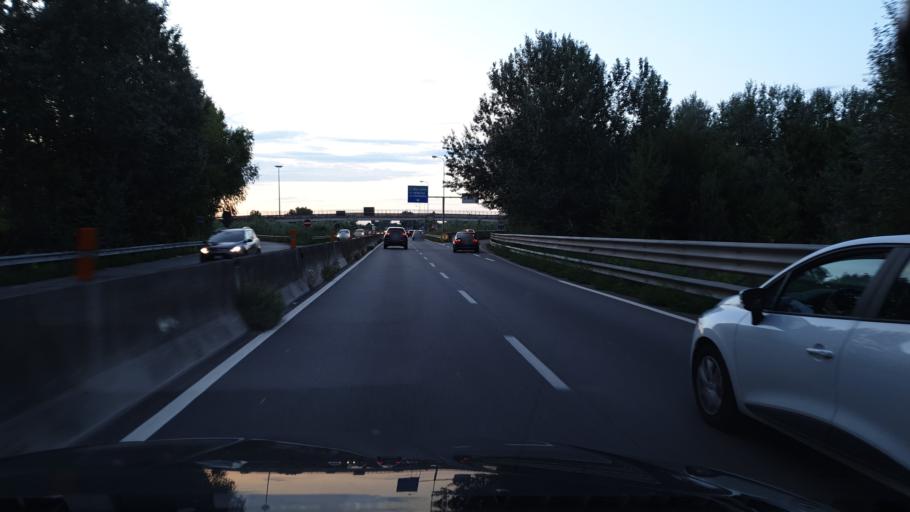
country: IT
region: Emilia-Romagna
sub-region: Provincia di Ravenna
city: Ravenna
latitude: 44.4085
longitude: 12.1743
